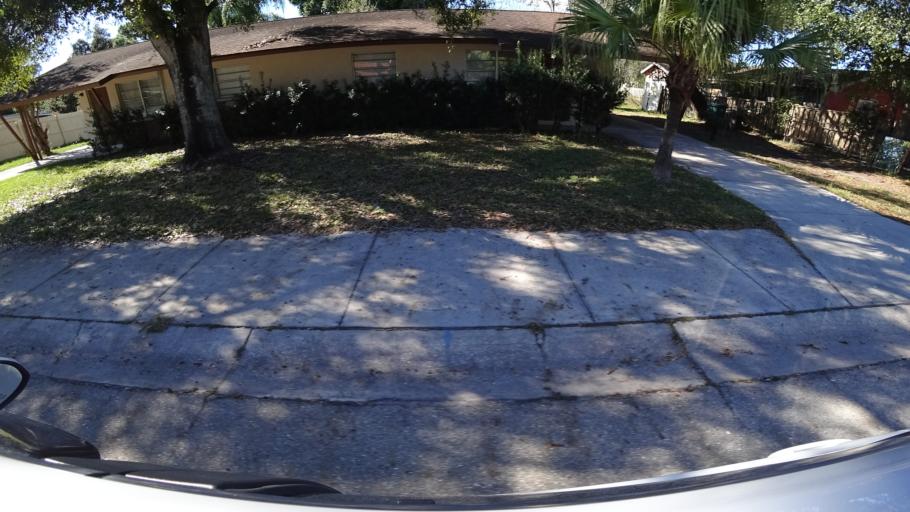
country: US
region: Florida
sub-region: Manatee County
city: West Samoset
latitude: 27.4397
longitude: -82.5523
